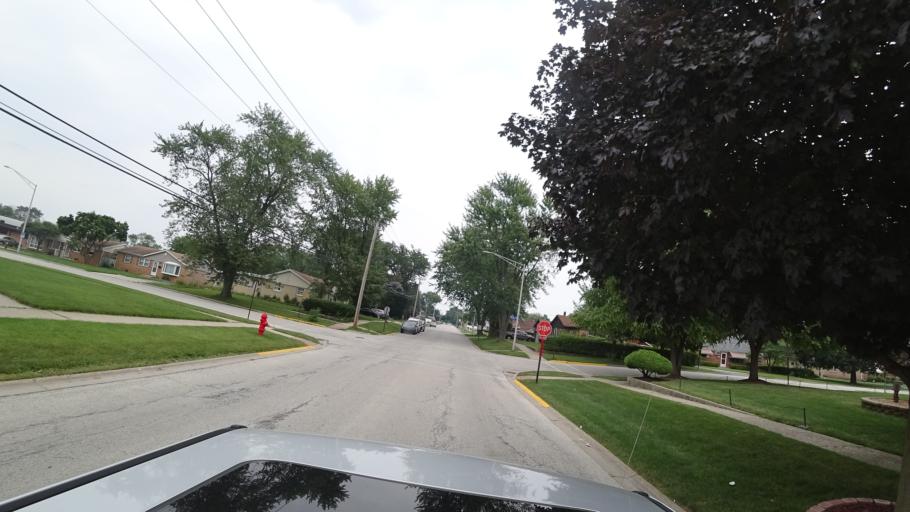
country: US
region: Illinois
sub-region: Cook County
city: Chicago Ridge
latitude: 41.6941
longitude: -87.7732
